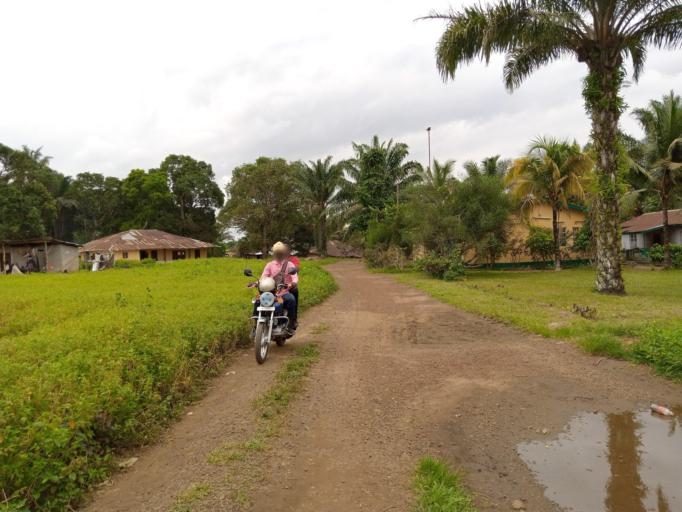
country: SL
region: Southern Province
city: Moyamba
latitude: 8.1627
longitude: -12.4261
